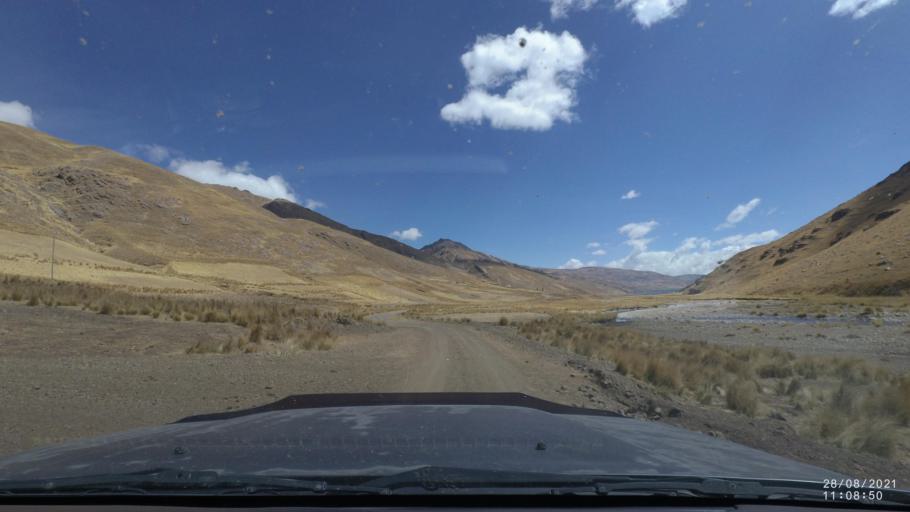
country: BO
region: Cochabamba
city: Cochabamba
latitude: -17.1645
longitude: -66.3048
